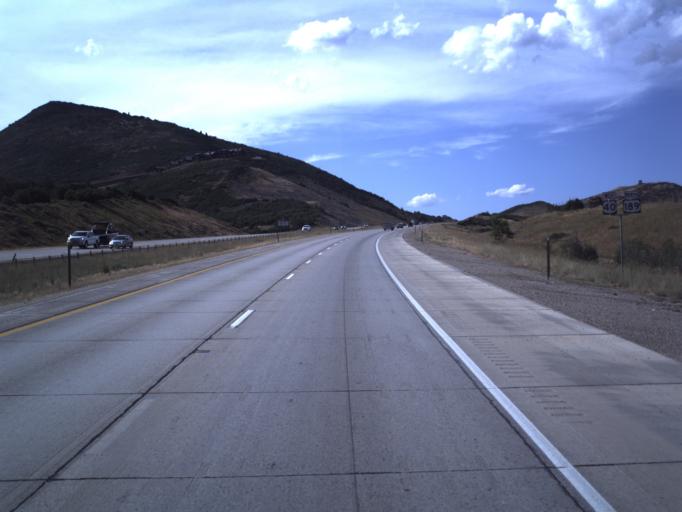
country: US
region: Utah
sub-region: Summit County
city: Park City
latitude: 40.6328
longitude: -111.4482
